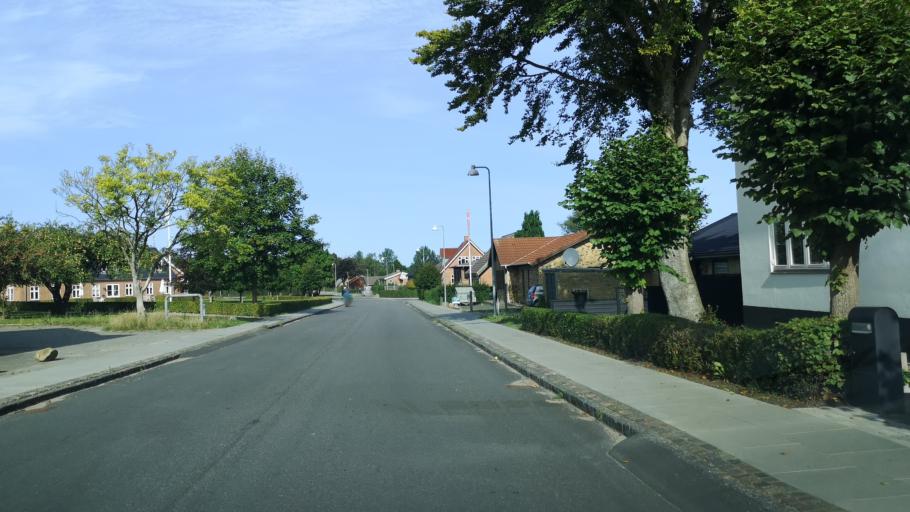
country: DK
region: Central Jutland
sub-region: Ikast-Brande Kommune
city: Ikast
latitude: 56.1461
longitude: 9.1531
